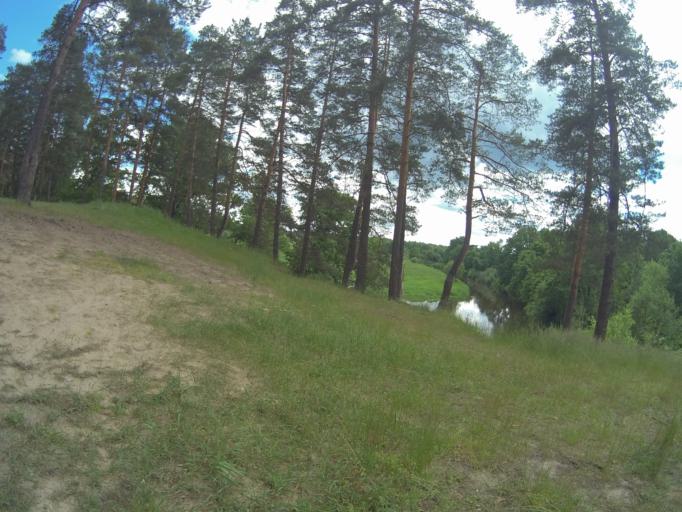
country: RU
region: Vladimir
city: Sudogda
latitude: 56.1442
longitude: 40.8156
